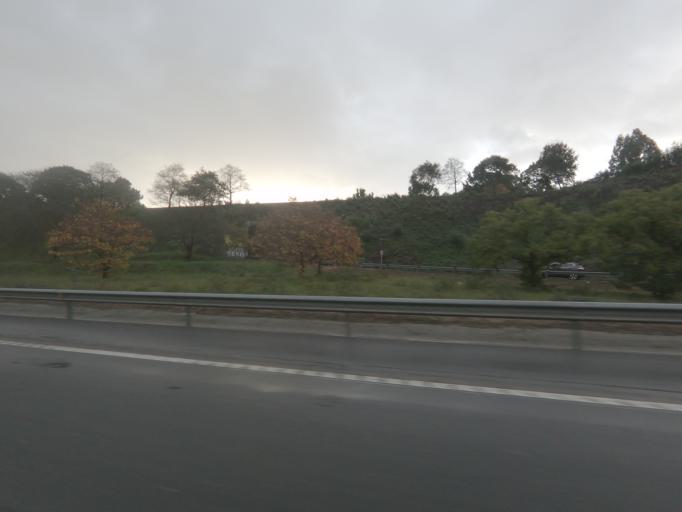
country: ES
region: Galicia
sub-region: Provincia de Pontevedra
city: Porrino
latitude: 42.2118
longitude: -8.6605
